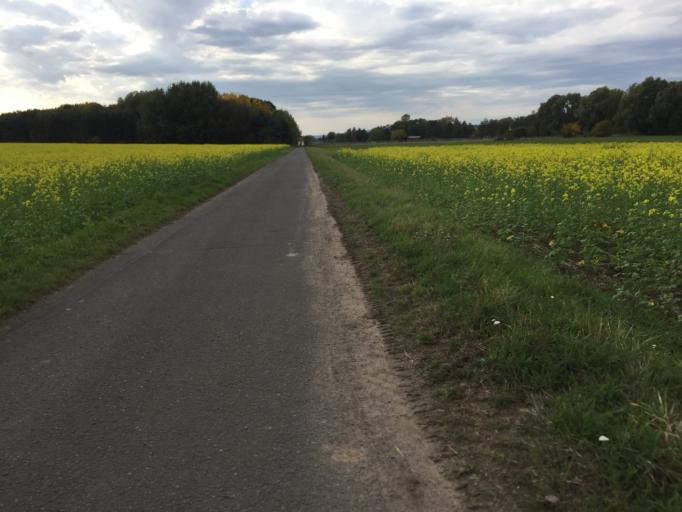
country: DE
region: Hesse
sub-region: Regierungsbezirk Giessen
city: Alten Buseck
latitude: 50.6082
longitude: 8.7625
